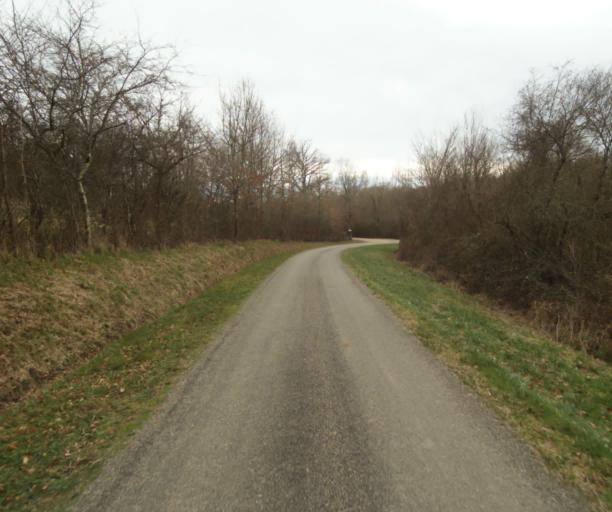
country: FR
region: Midi-Pyrenees
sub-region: Departement du Gers
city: Eauze
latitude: 43.9203
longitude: 0.0635
